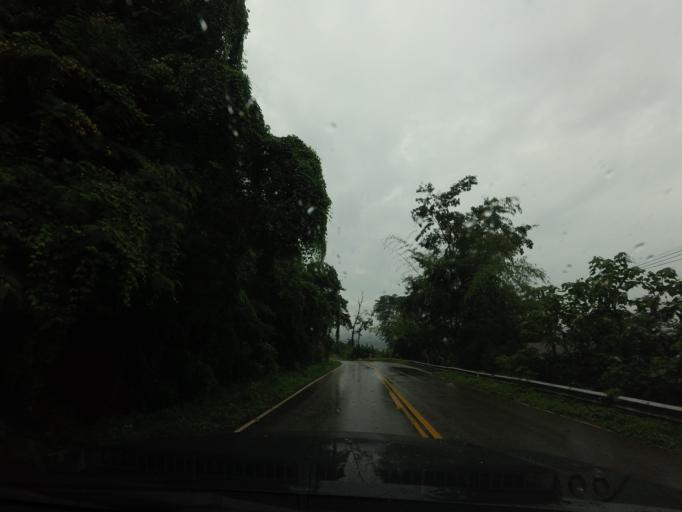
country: TH
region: Nong Khai
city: Sangkhom
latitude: 18.2118
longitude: 102.0958
